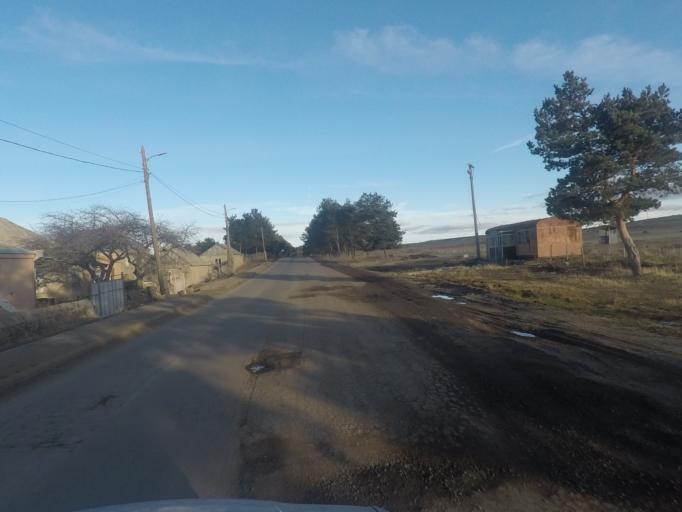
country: GE
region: Kvemo Kartli
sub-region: Tsalka
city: Tsalka
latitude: 41.6029
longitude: 44.0592
